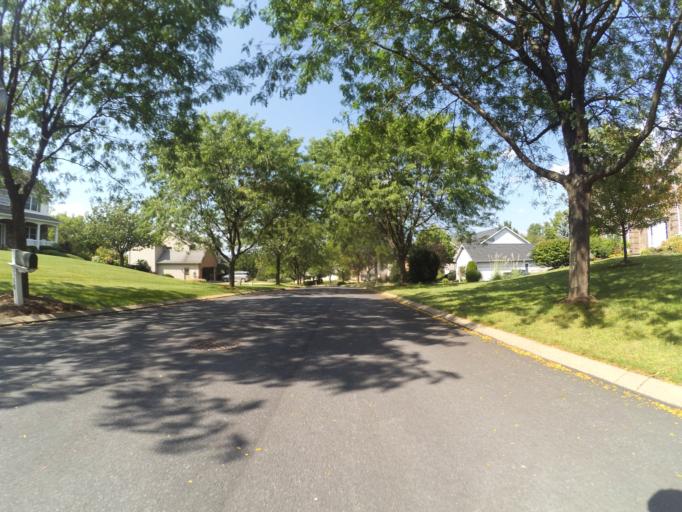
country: US
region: Pennsylvania
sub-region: Centre County
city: Houserville
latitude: 40.8153
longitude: -77.8278
